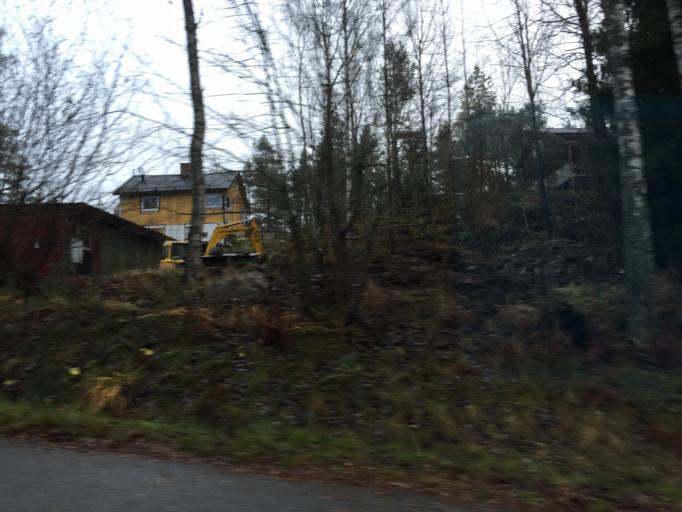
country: SE
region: Stockholm
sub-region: Nynashamns Kommun
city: Osmo
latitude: 59.0289
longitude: 17.9281
